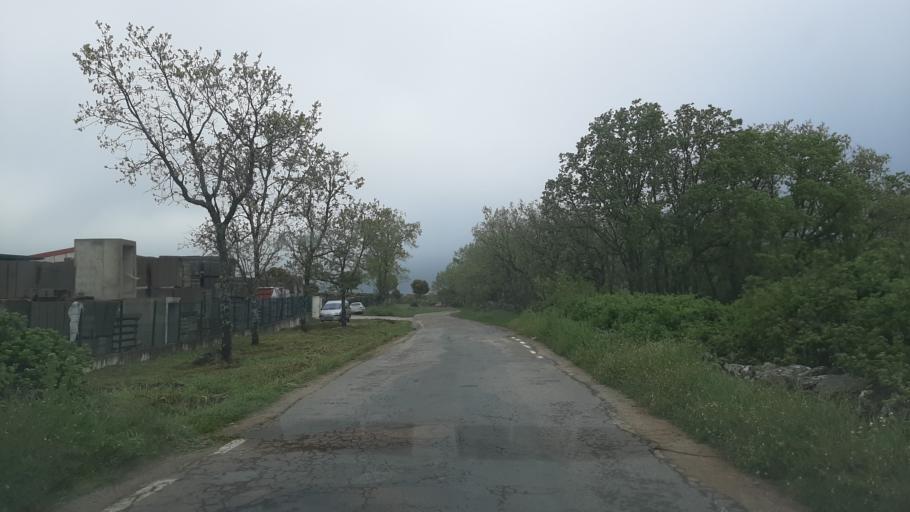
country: ES
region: Castille and Leon
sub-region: Provincia de Salamanca
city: Endrinal
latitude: 40.5546
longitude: -5.8070
